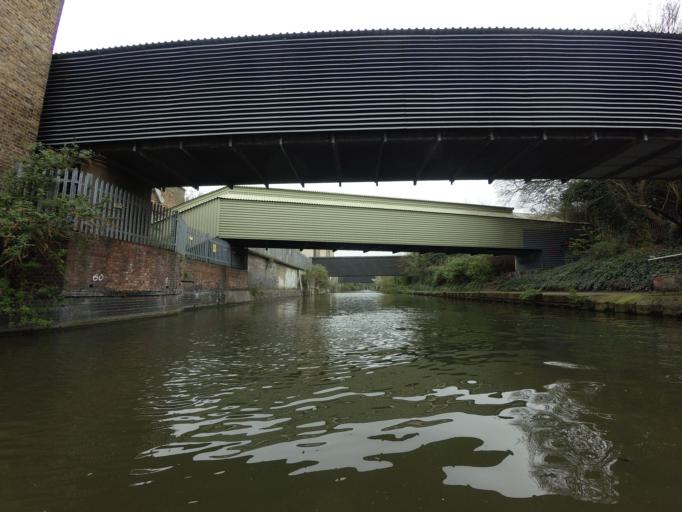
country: GB
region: England
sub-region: Greater London
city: Acton
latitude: 51.5336
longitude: -0.2579
